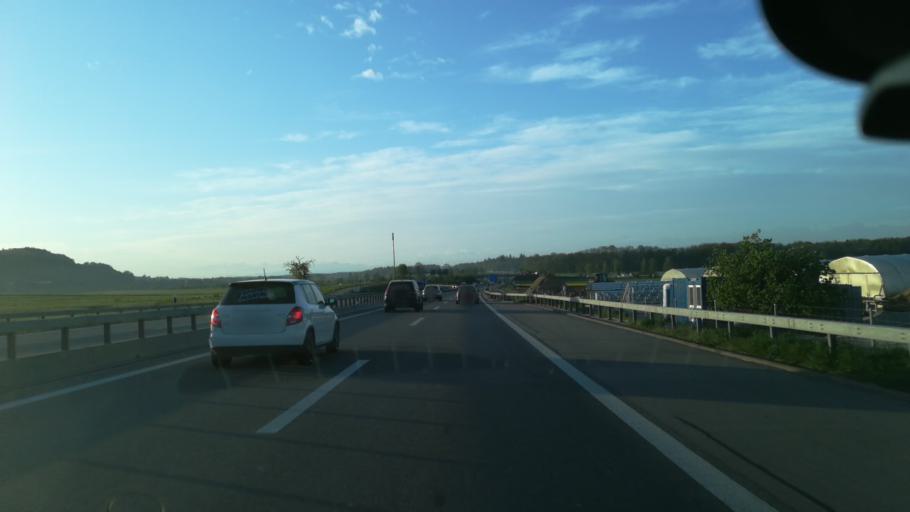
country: CH
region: Zurich
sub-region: Bezirk Andelfingen
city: Marthalen
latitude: 47.6499
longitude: 8.6463
